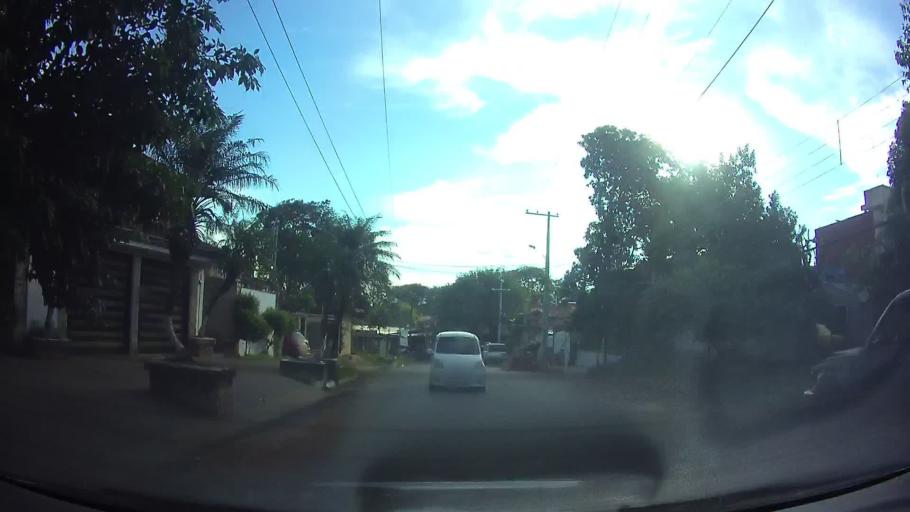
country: PY
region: Central
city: Villa Elisa
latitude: -25.3610
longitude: -57.5926
